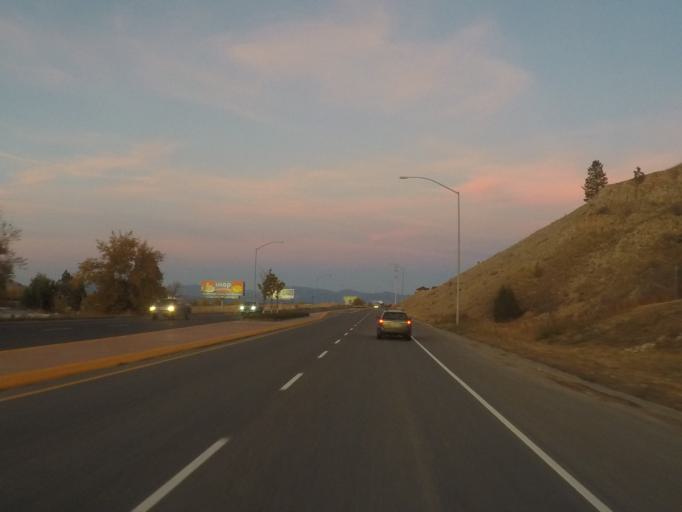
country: US
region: Montana
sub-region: Lewis and Clark County
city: Helena West Side
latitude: 46.6038
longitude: -112.0858
